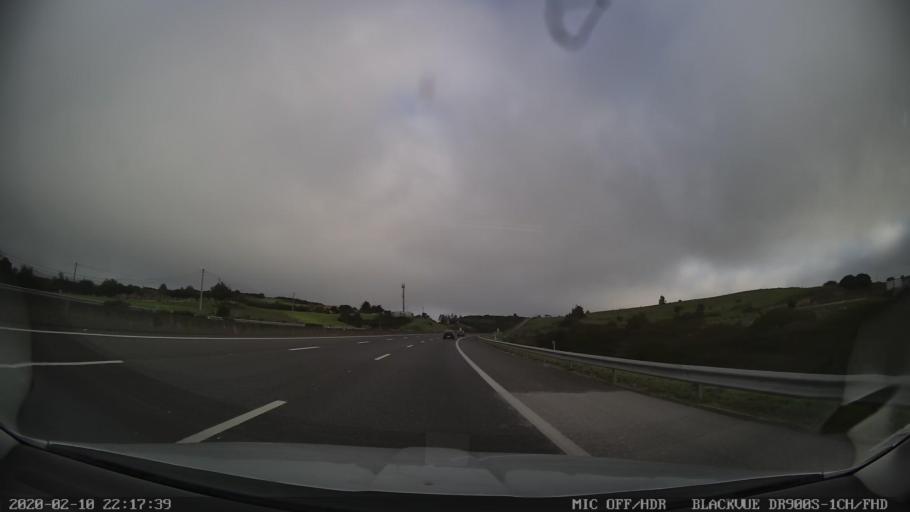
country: PT
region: Lisbon
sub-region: Loures
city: Bucelas
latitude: 38.9213
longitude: -9.0751
